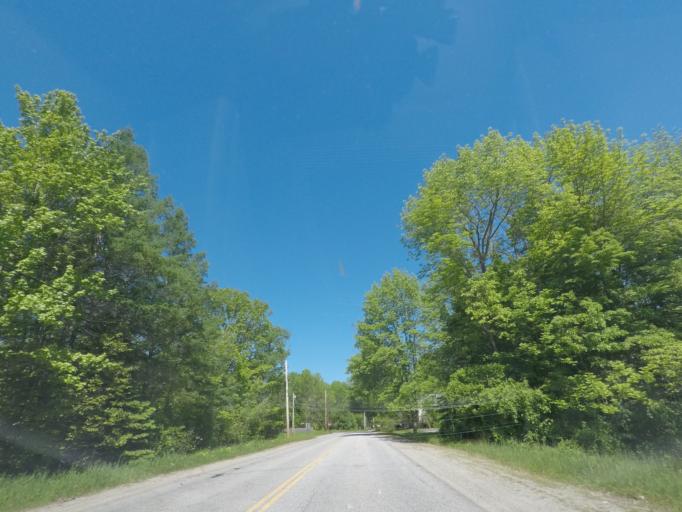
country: US
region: Maine
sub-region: Kennebec County
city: Manchester
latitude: 44.2353
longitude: -69.8862
